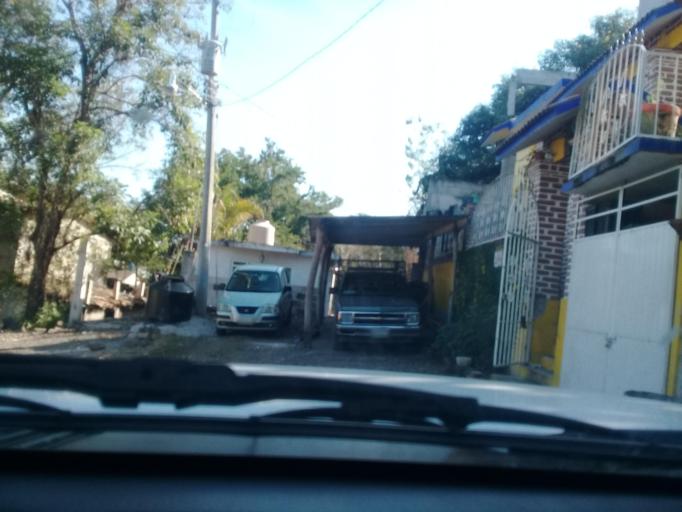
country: MX
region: Veracruz
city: Actopan
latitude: 19.4975
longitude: -96.6068
